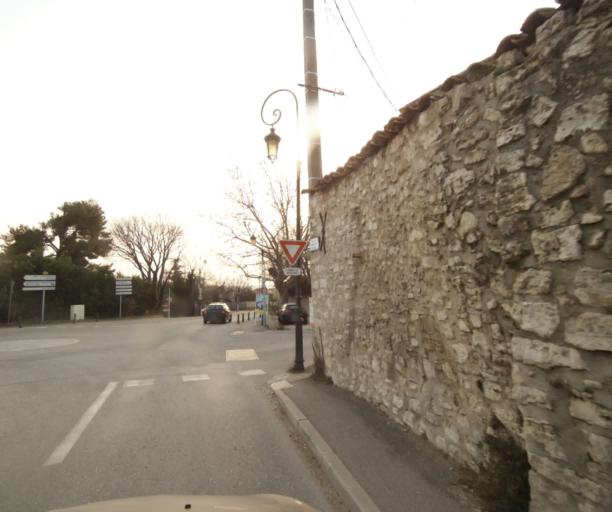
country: FR
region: Provence-Alpes-Cote d'Azur
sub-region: Departement des Bouches-du-Rhone
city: Eguilles
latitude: 43.5719
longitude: 5.3606
